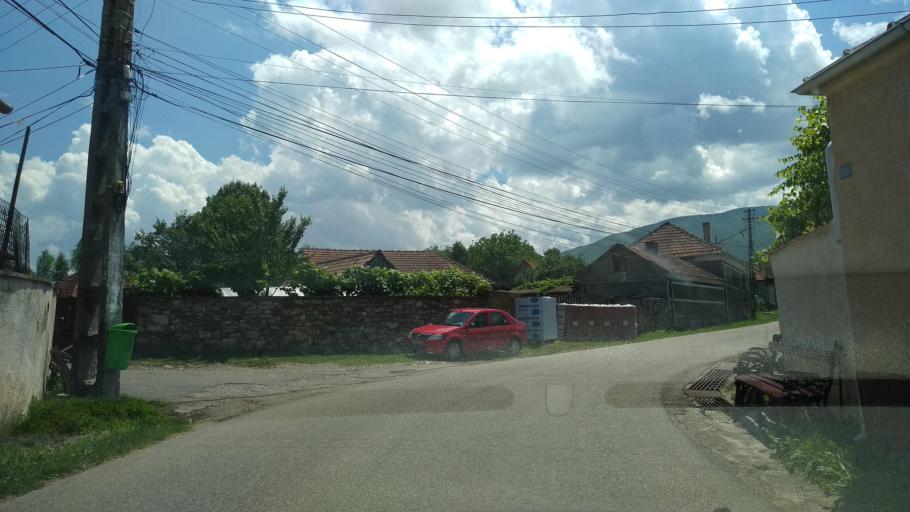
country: RO
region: Hunedoara
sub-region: Comuna Sarmizegetusa
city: Sarmizegetusa
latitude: 45.5143
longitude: 22.7817
